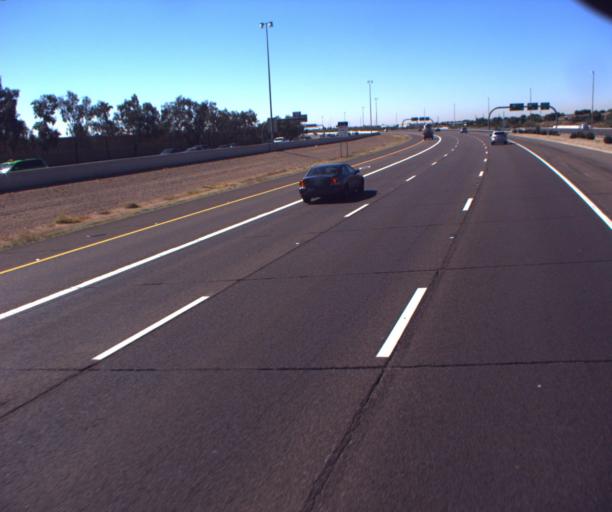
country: US
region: Arizona
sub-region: Maricopa County
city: Sun City
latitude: 33.6658
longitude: -112.2282
